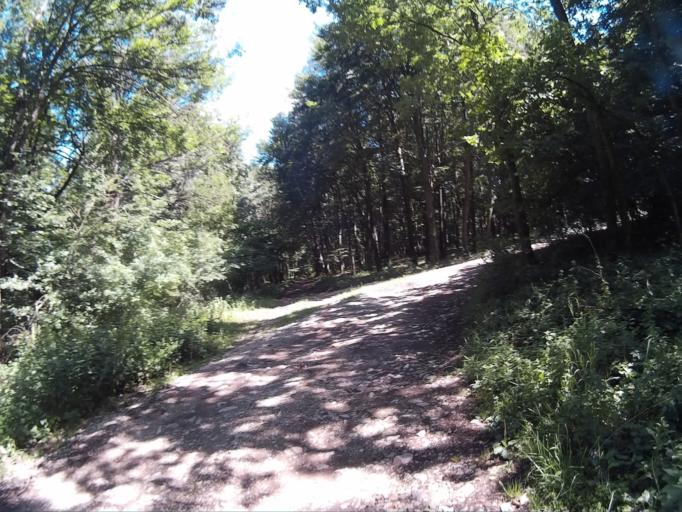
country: HU
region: Veszprem
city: Urkut
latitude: 47.1175
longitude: 17.6861
